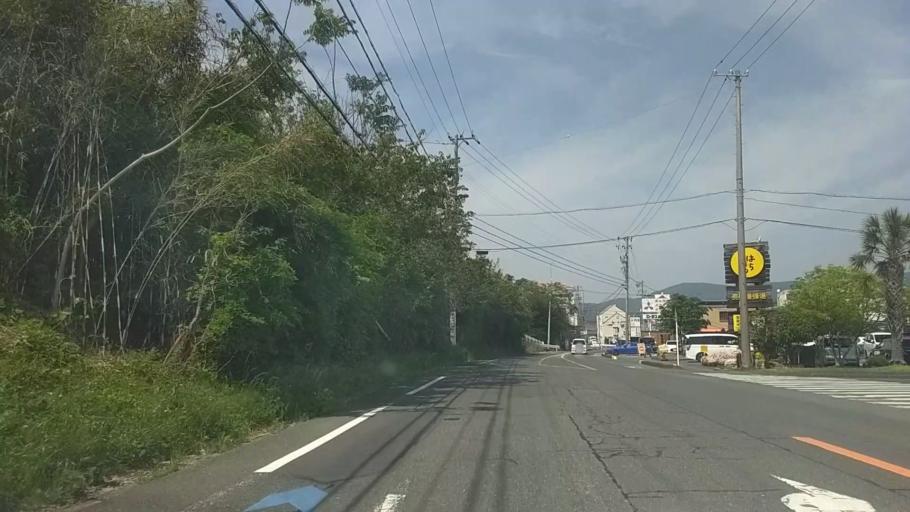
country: JP
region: Shizuoka
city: Kosai-shi
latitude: 34.7918
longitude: 137.5460
